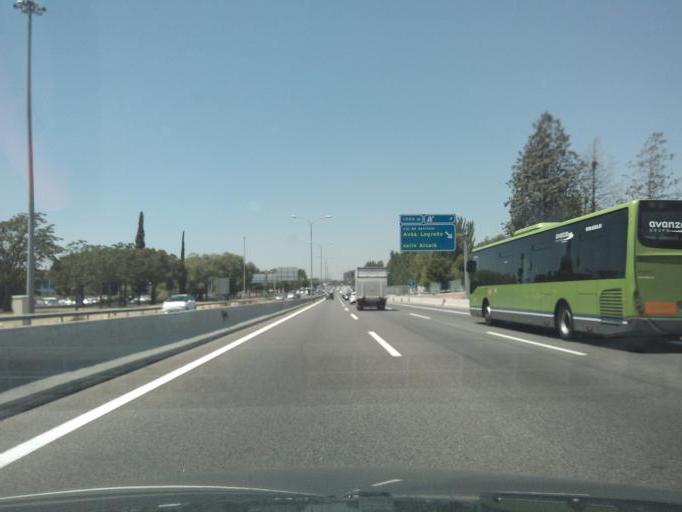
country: ES
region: Madrid
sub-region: Provincia de Madrid
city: Barajas de Madrid
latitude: 40.4500
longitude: -3.5904
